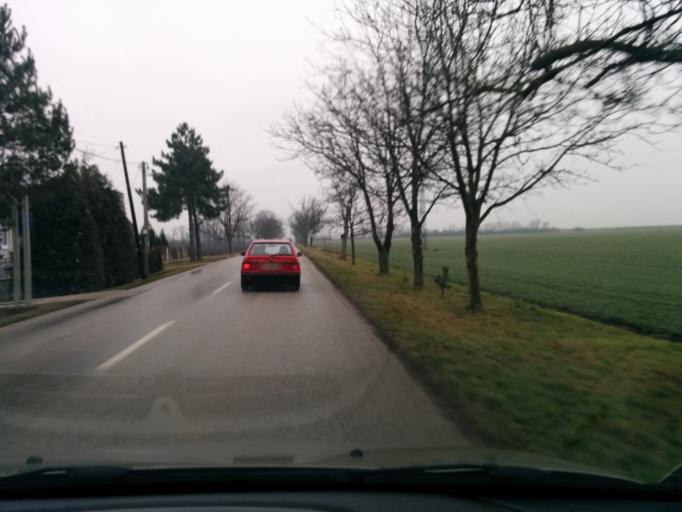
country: SK
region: Trnavsky
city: Sladkovicovo
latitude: 48.2393
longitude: 17.6256
